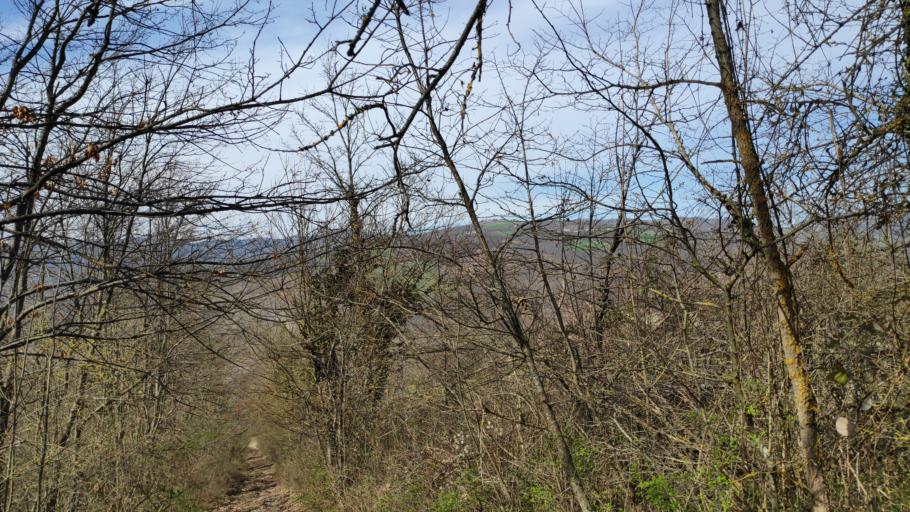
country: IT
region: Emilia-Romagna
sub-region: Provincia di Bologna
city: Berzantina
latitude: 44.1764
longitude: 10.9957
